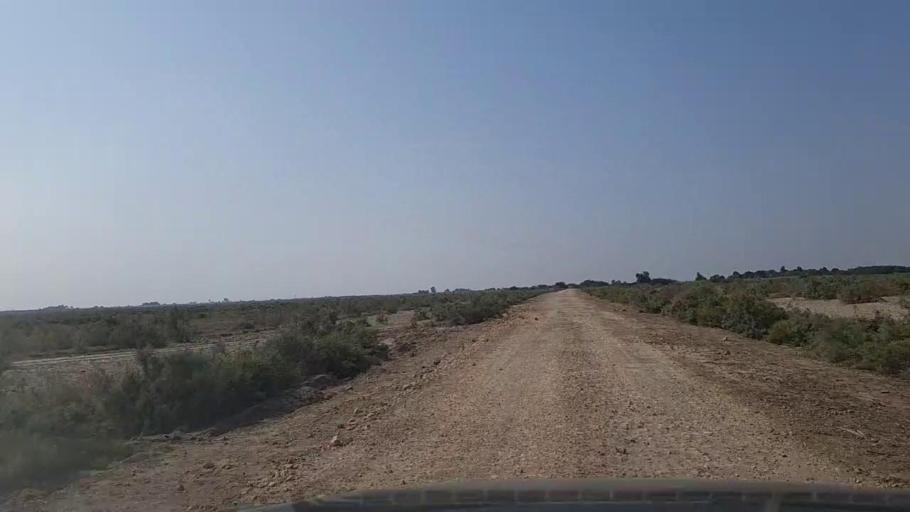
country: PK
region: Sindh
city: Mirpur Sakro
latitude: 24.4314
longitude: 67.7236
